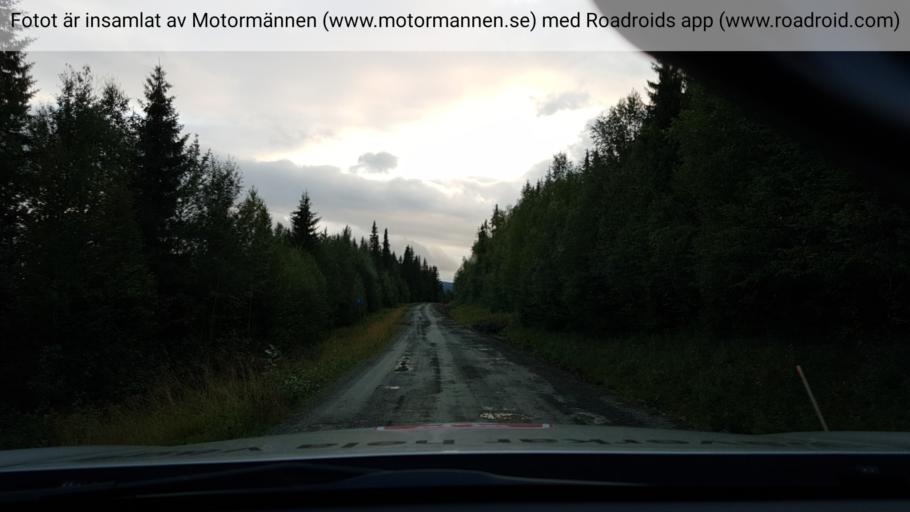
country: SE
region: Vaesterbotten
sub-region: Vilhelmina Kommun
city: Sjoberg
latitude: 65.4983
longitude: 15.5373
